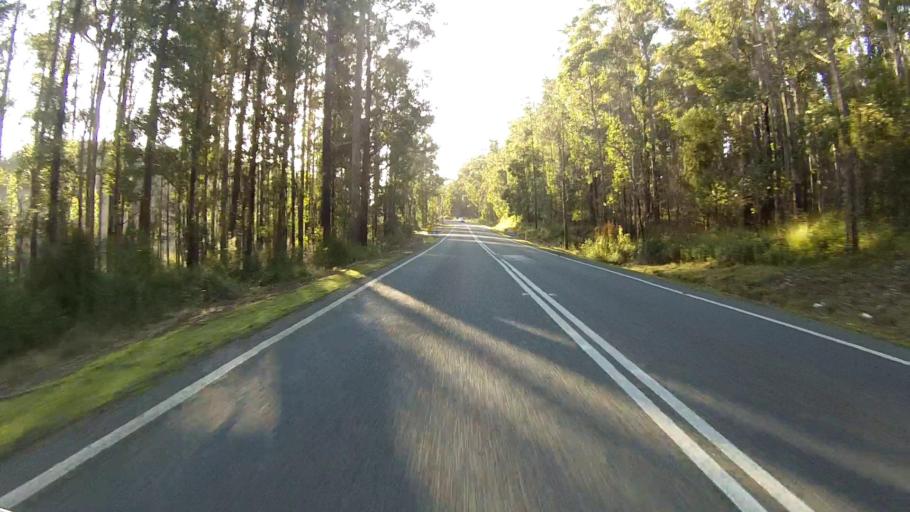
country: AU
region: Tasmania
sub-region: Sorell
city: Sorell
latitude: -42.9815
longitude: 147.9105
